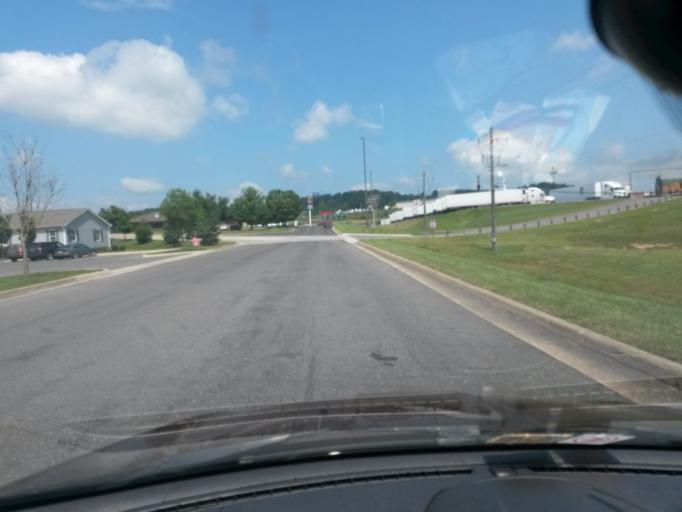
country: US
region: Virginia
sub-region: Augusta County
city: Stuarts Draft
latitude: 37.9274
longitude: -79.2285
